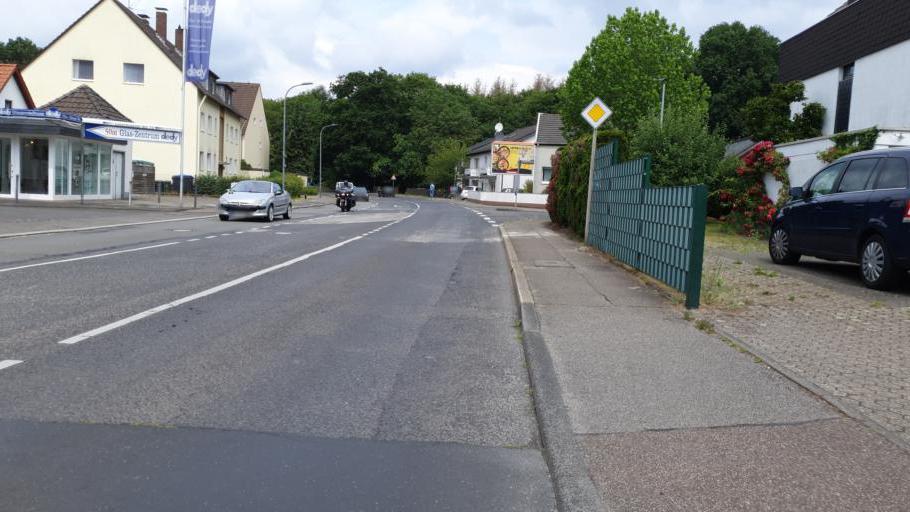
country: DE
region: North Rhine-Westphalia
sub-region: Regierungsbezirk Koln
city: Odenthal
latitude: 51.0201
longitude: 7.0728
